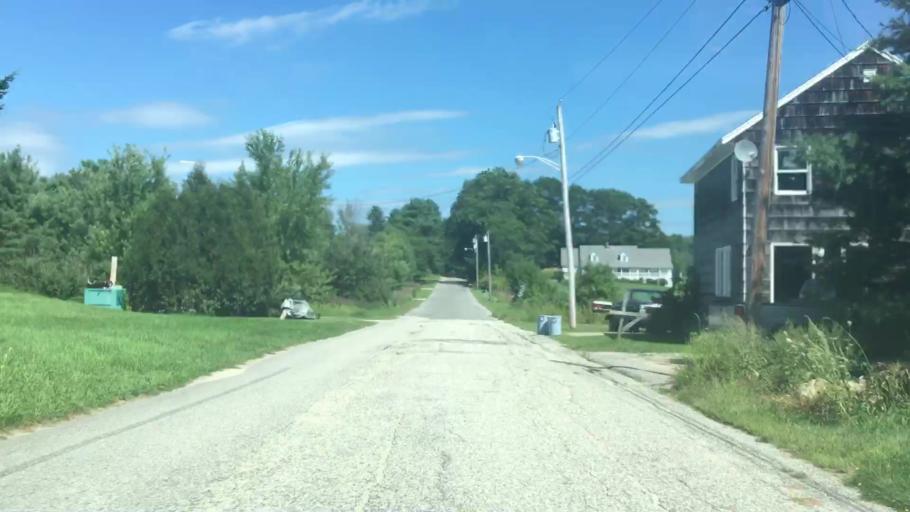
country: US
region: Maine
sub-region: Androscoggin County
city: Sabattus
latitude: 44.1019
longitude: -70.1285
